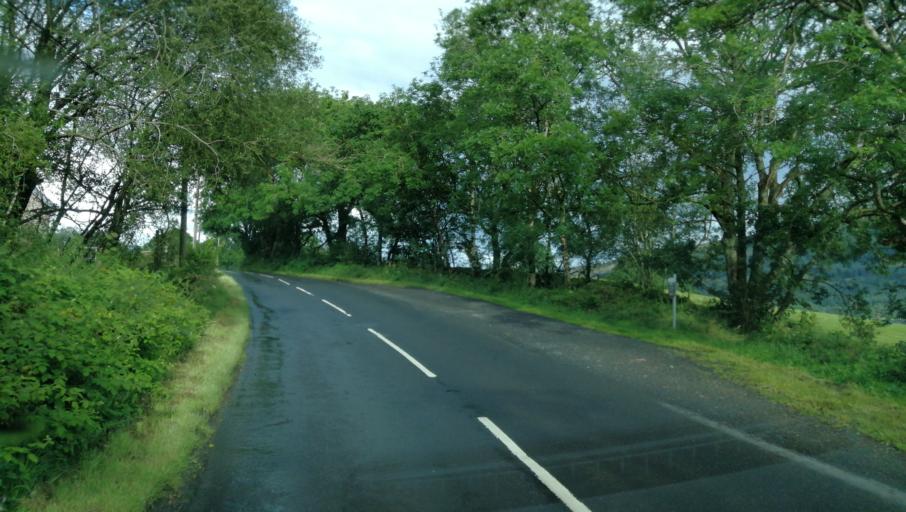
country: GB
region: Scotland
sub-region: Stirling
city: Callander
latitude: 56.2255
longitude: -4.3003
